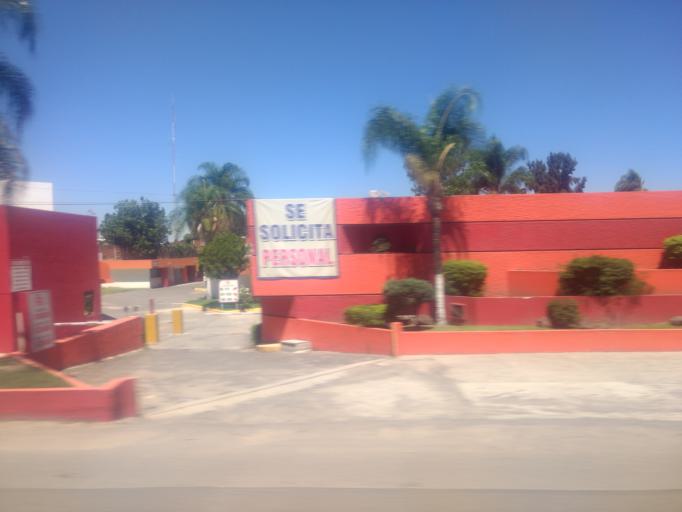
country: MX
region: Jalisco
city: Nicolas R Casillas
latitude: 20.5391
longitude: -103.4738
